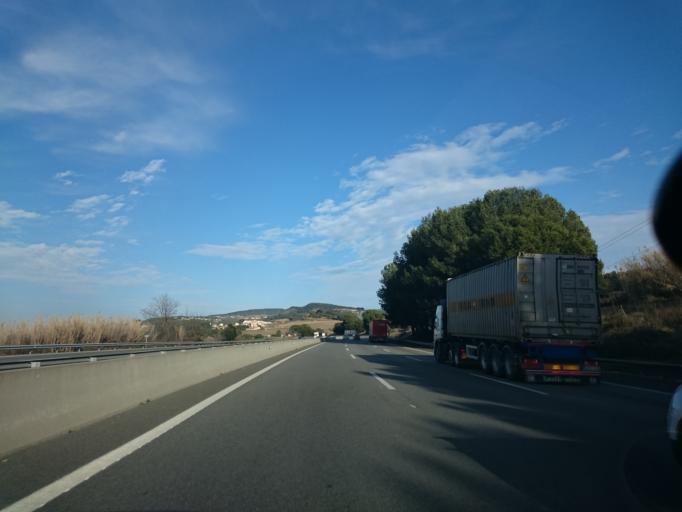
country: ES
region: Catalonia
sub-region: Provincia de Barcelona
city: La Granada
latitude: 41.3864
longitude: 1.7486
